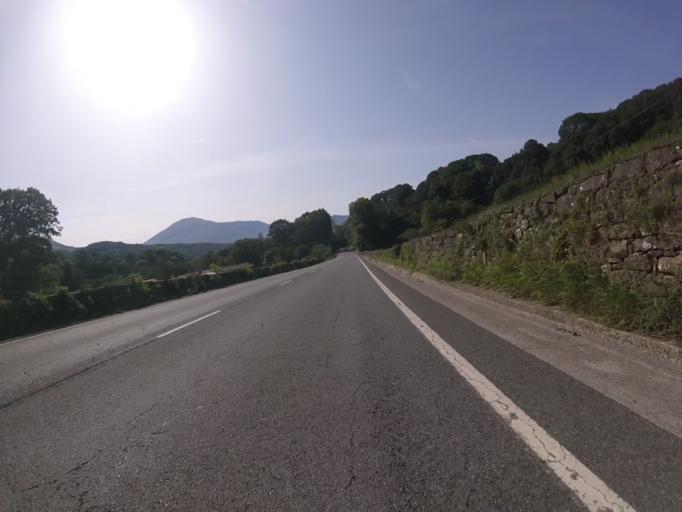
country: ES
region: Navarre
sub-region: Provincia de Navarra
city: Zugarramurdi
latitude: 43.2042
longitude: -1.4859
